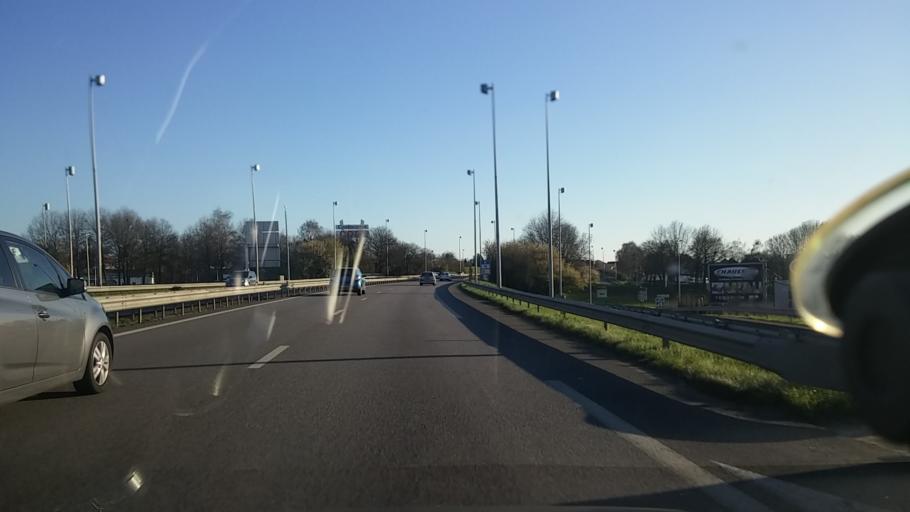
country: FR
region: Limousin
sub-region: Departement de la Haute-Vienne
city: Rilhac-Rancon
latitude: 45.8844
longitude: 1.2914
